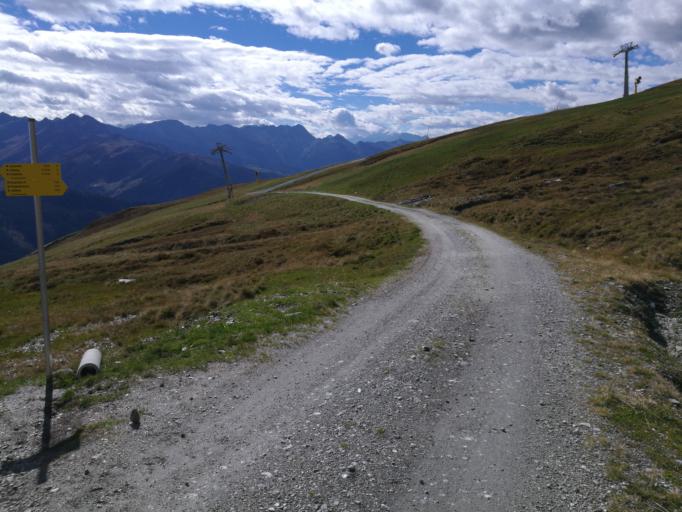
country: AT
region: Salzburg
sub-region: Politischer Bezirk Zell am See
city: Krimml
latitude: 47.2568
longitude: 12.0980
